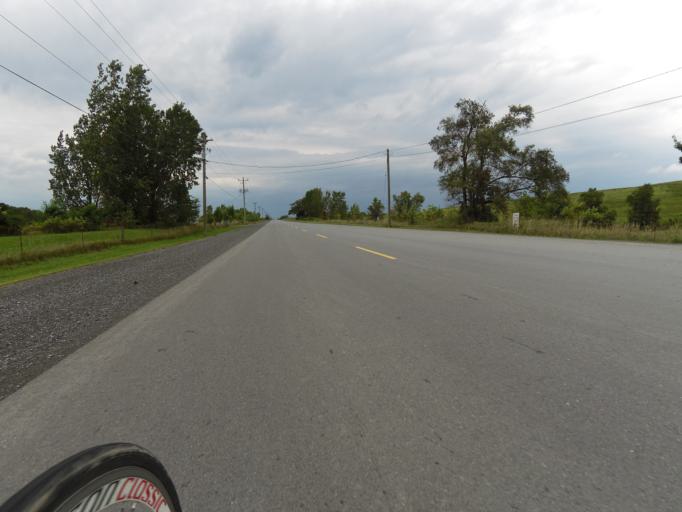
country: CA
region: Ontario
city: Bells Corners
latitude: 45.2272
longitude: -75.7783
